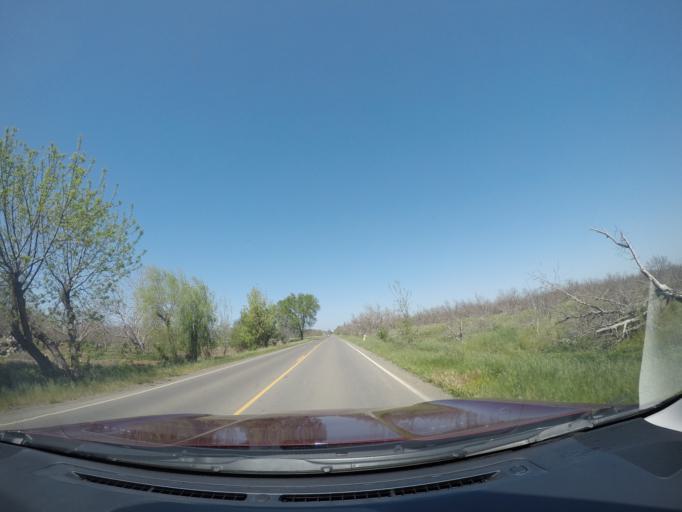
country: US
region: California
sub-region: Yolo County
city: Winters
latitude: 38.4989
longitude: -121.9548
